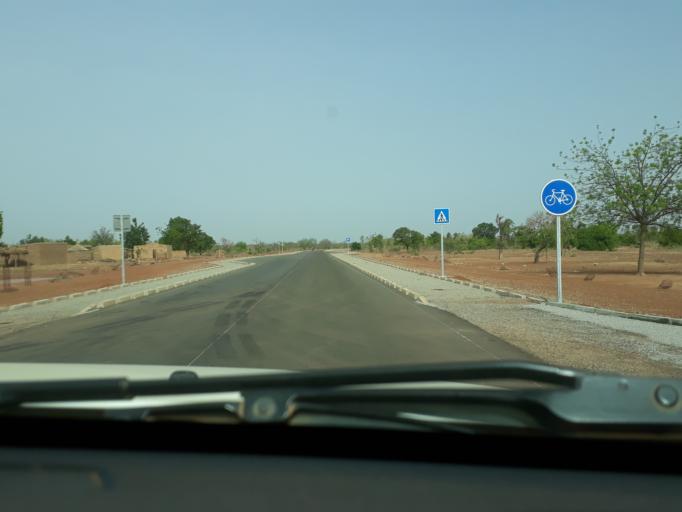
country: BF
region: Plateau-Central
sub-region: Province d'Oubritenga
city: Ziniare
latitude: 12.5500
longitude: -1.3964
